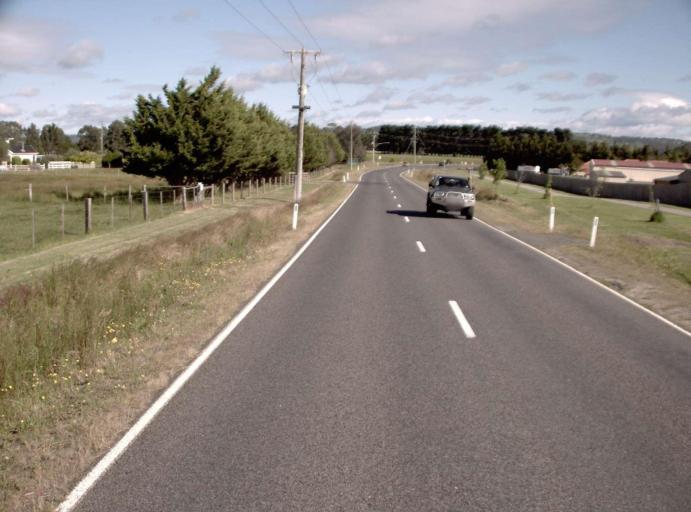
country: AU
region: Victoria
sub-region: Latrobe
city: Traralgon
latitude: -38.1843
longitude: 146.5016
